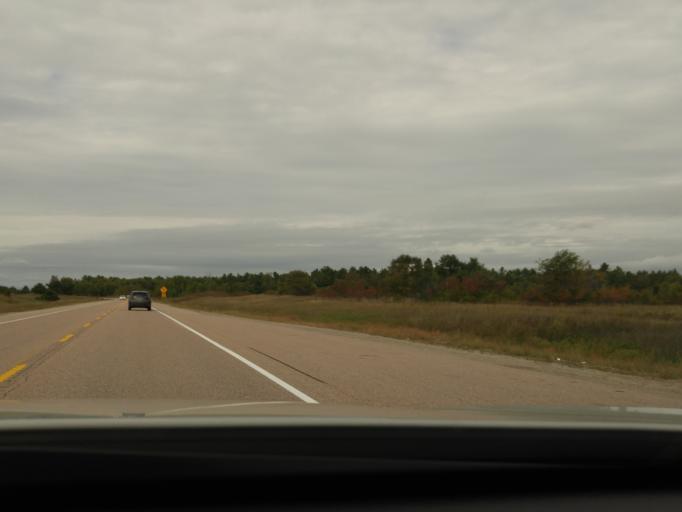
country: CA
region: Ontario
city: Renfrew
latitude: 45.5715
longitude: -76.7787
